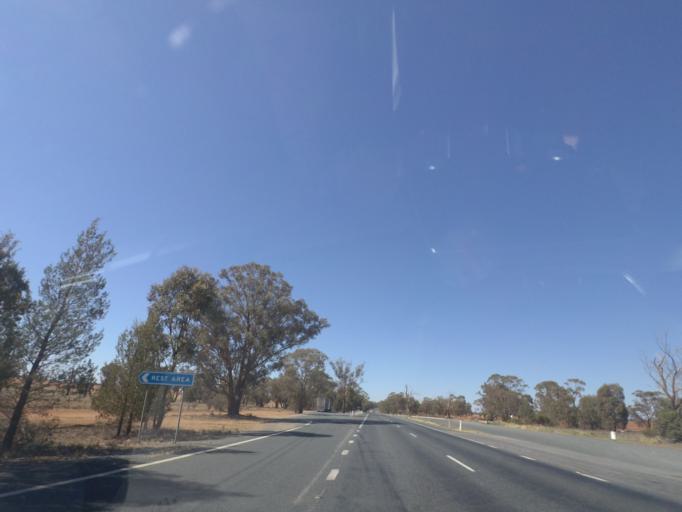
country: AU
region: New South Wales
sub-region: Bland
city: West Wyalong
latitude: -34.1985
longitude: 147.1106
